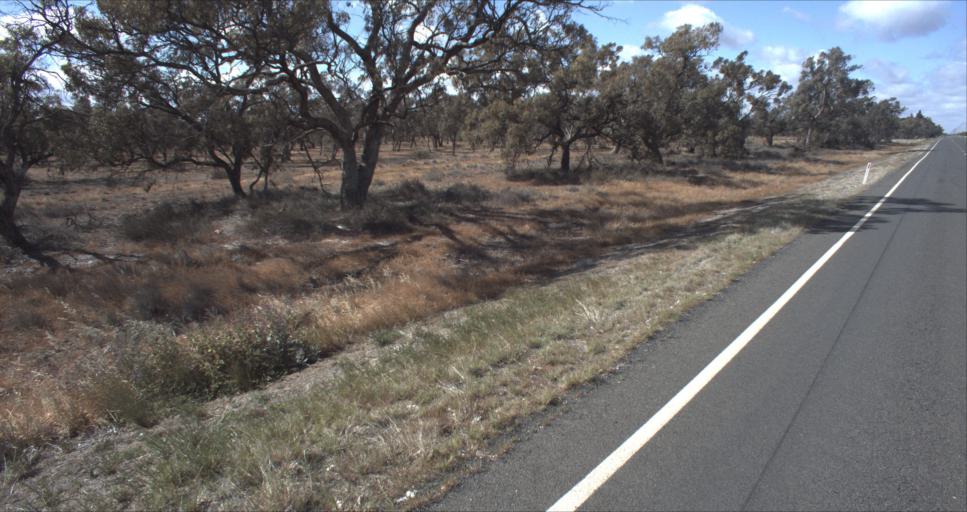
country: AU
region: New South Wales
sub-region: Murrumbidgee Shire
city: Darlington Point
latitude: -34.5237
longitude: 146.1752
